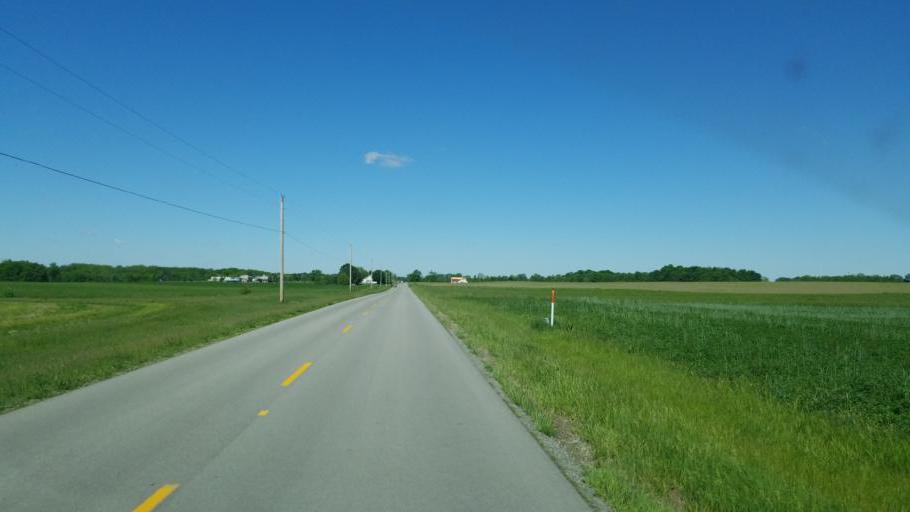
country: US
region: Ohio
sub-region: Logan County
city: Russells Point
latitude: 40.4249
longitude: -83.8611
